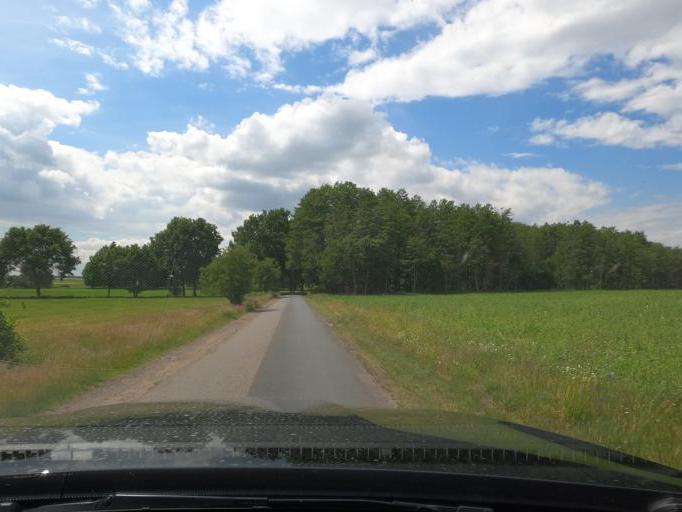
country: DE
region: Lower Saxony
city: Steimbke
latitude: 52.6291
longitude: 9.4169
